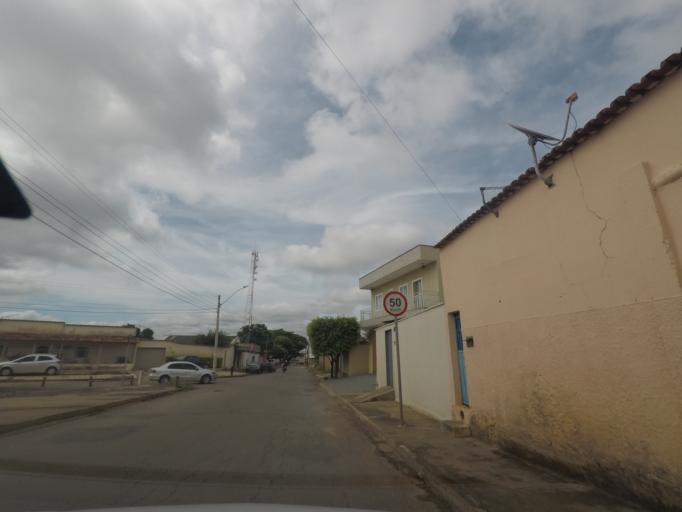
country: BR
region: Goias
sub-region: Goiania
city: Goiania
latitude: -16.6646
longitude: -49.1852
